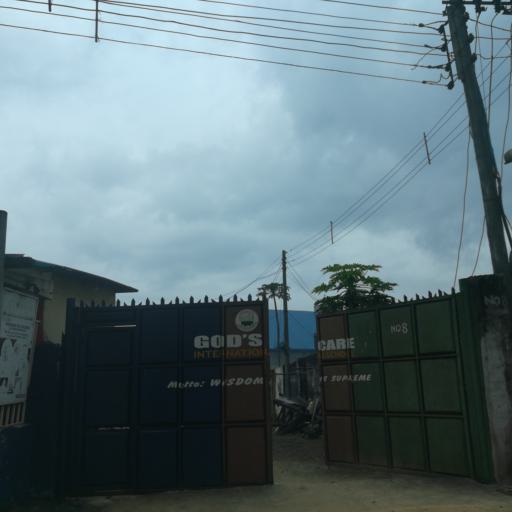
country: NG
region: Rivers
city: Port Harcourt
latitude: 4.8251
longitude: 7.0412
